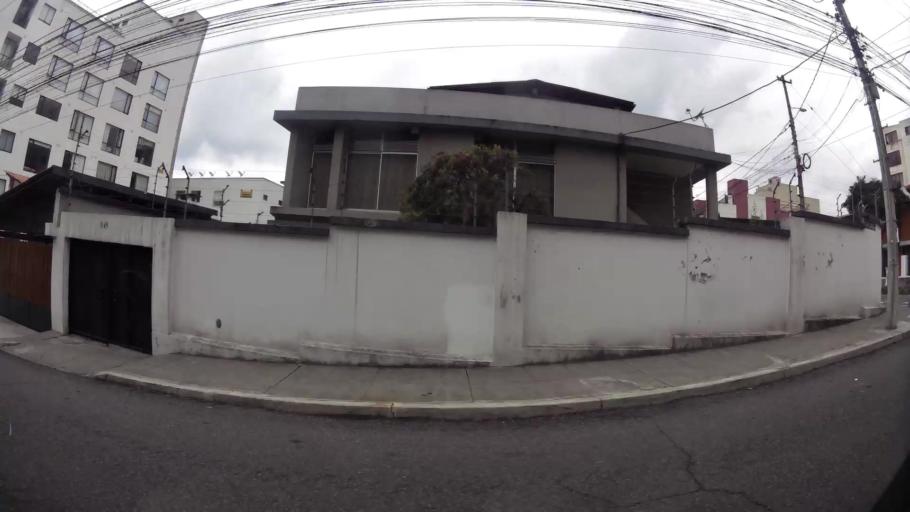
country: EC
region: Pichincha
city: Quito
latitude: -0.1708
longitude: -78.4952
